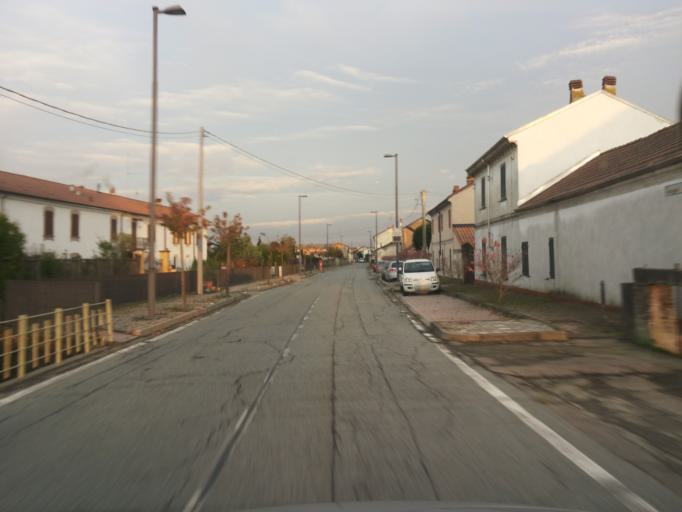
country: IT
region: Piedmont
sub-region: Provincia di Vercelli
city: Pezzana
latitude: 45.2603
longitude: 8.4754
